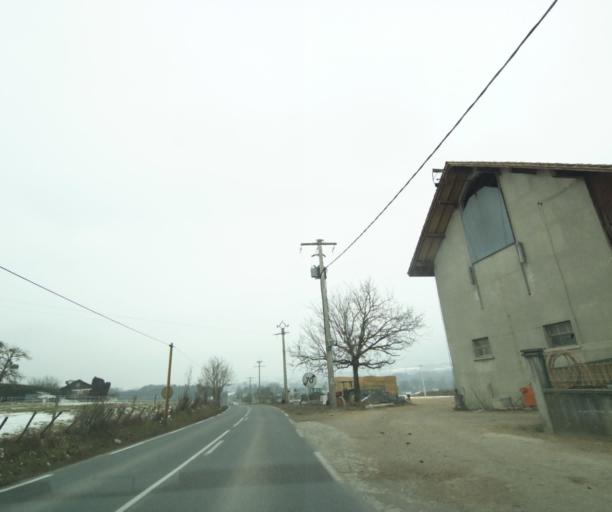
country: FR
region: Rhone-Alpes
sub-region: Departement de la Haute-Savoie
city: Contamine-sur-Arve
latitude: 46.1243
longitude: 6.3138
